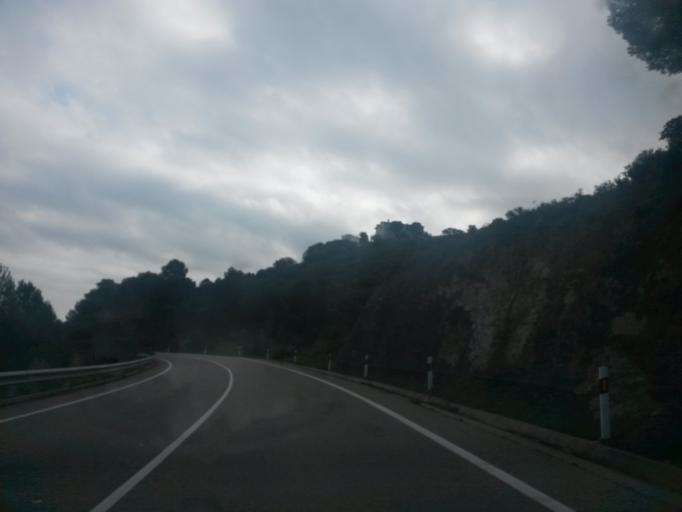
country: ES
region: Catalonia
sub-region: Provincia de Girona
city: Colera
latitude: 42.3900
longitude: 3.1544
